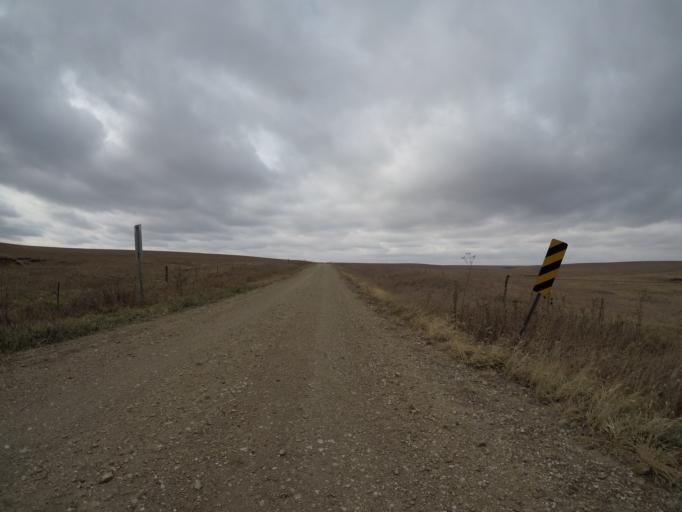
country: US
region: Kansas
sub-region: Morris County
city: Council Grove
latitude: 38.7245
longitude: -96.1967
